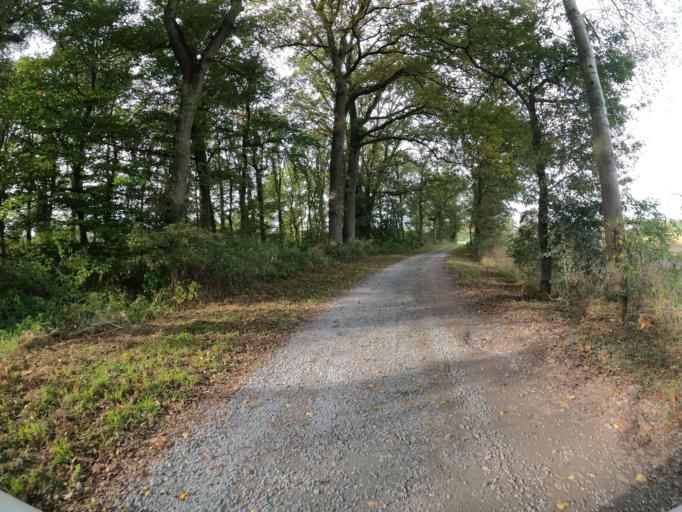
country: DE
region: North Rhine-Westphalia
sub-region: Regierungsbezirk Dusseldorf
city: Schermbeck
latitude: 51.7008
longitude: 6.8567
